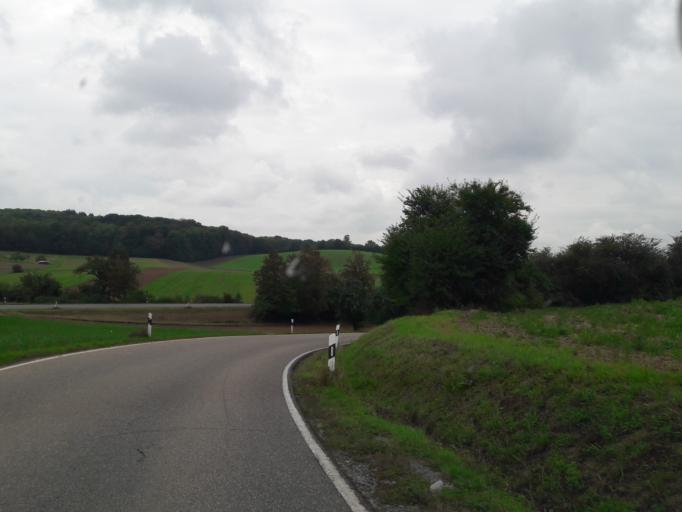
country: DE
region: Baden-Wuerttemberg
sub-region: Regierungsbezirk Stuttgart
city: Oedheim
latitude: 49.2140
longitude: 9.2874
